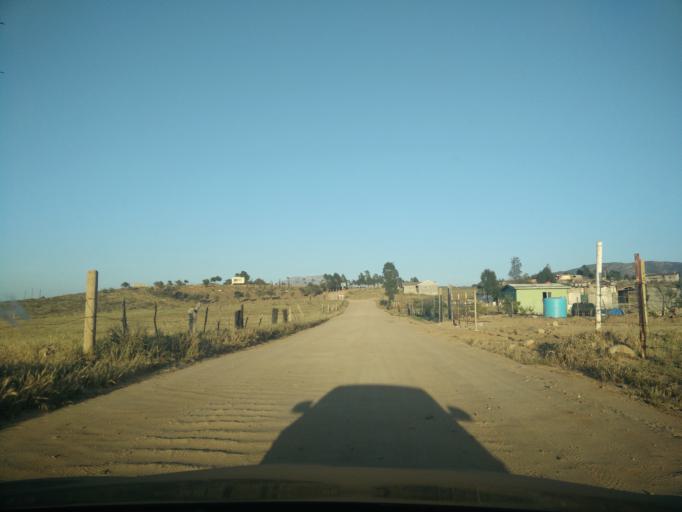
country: MX
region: Baja California
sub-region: Ensenada
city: Rancho Verde
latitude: 32.0450
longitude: -116.6487
